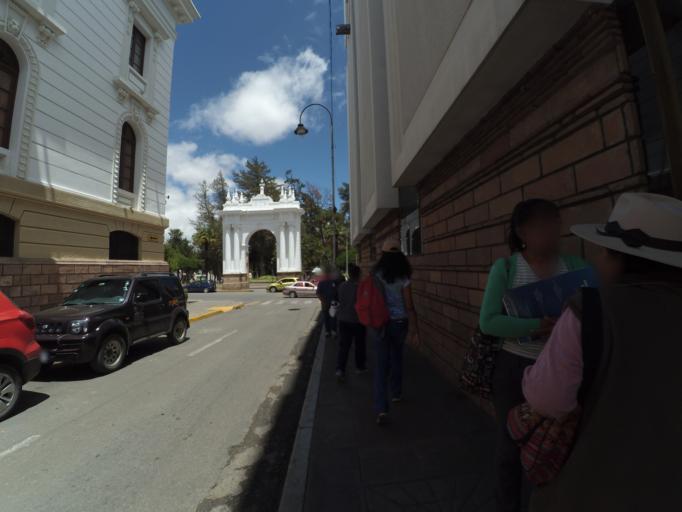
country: BO
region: Chuquisaca
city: Sucre
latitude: -19.0432
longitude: -65.2626
